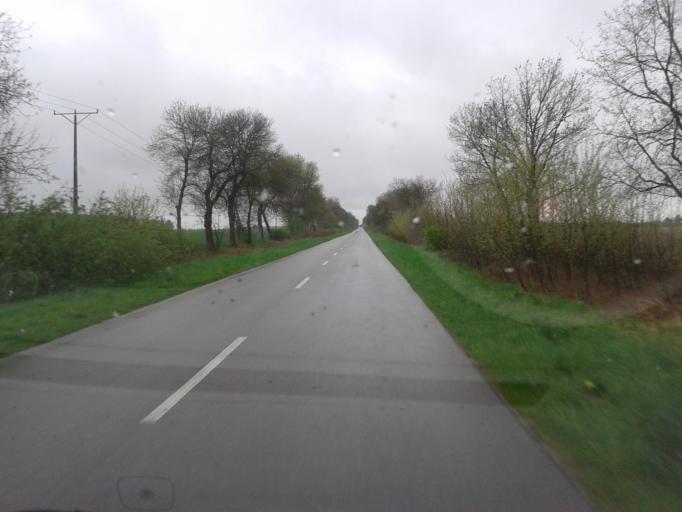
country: UA
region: Lviv
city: Uhniv
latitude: 50.4131
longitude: 23.7359
